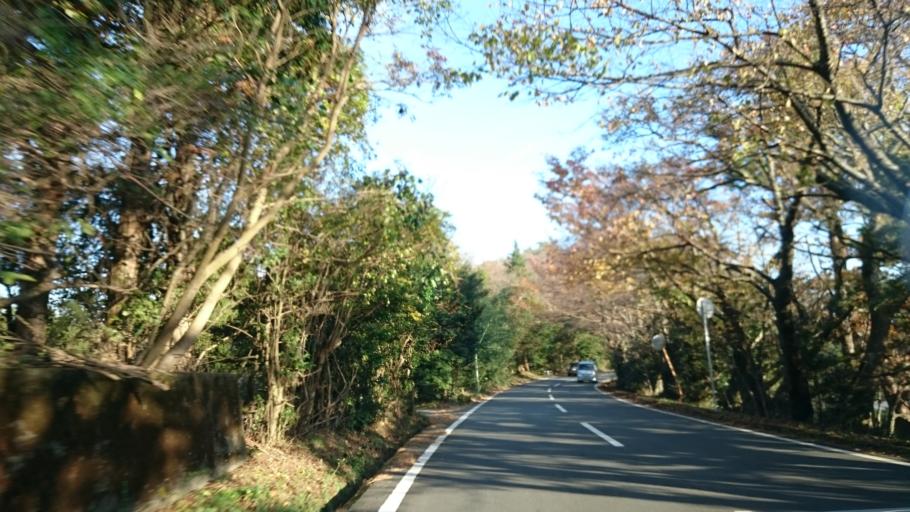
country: JP
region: Shizuoka
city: Heda
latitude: 34.9762
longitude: 138.8877
